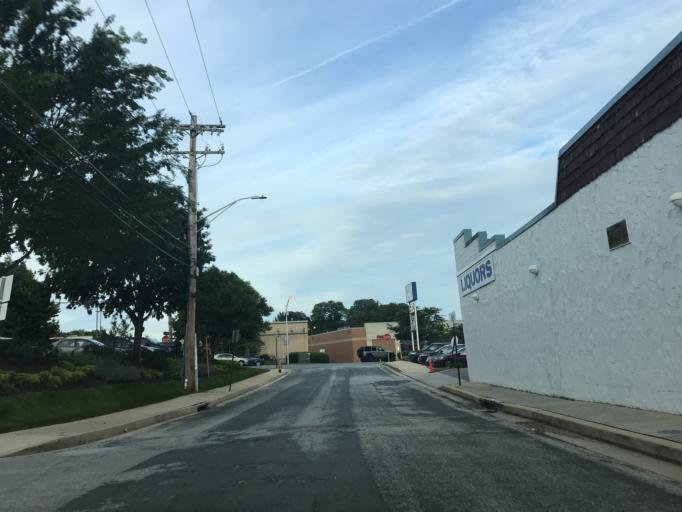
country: US
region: Maryland
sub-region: Baltimore County
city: Towson
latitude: 39.3721
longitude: -76.6106
